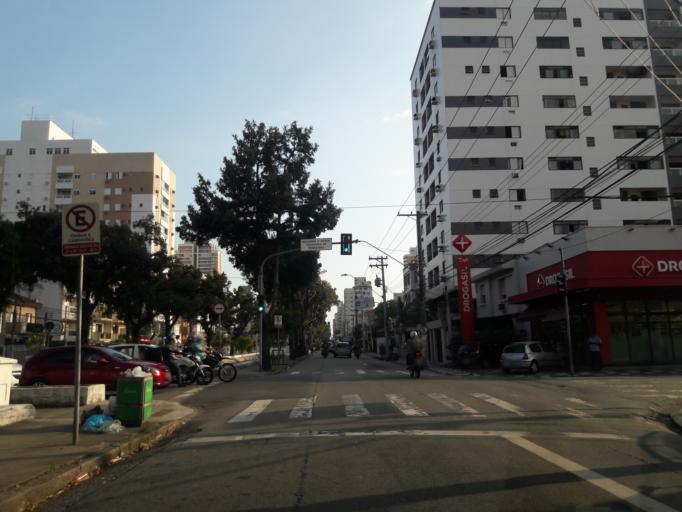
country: BR
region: Sao Paulo
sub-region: Santos
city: Santos
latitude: -23.9591
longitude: -46.3381
